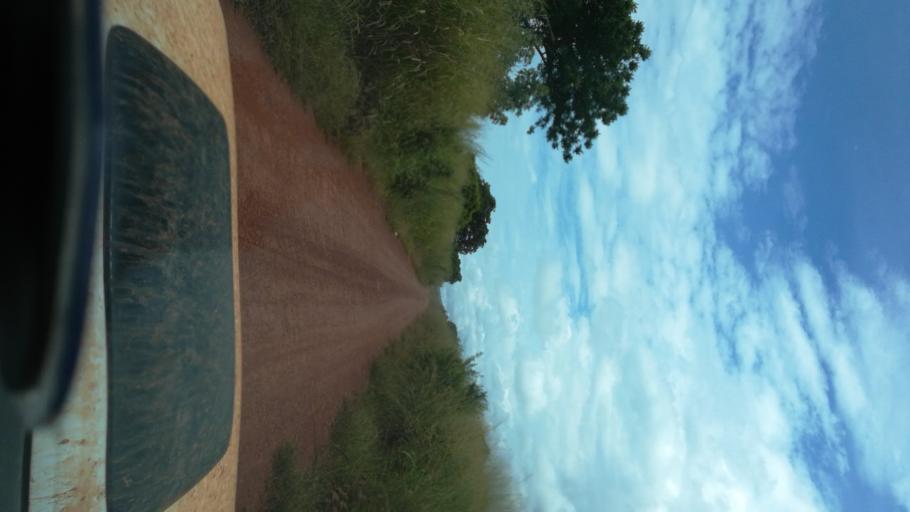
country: ZM
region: Northern
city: Kaputa
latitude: -8.5274
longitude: 28.8419
